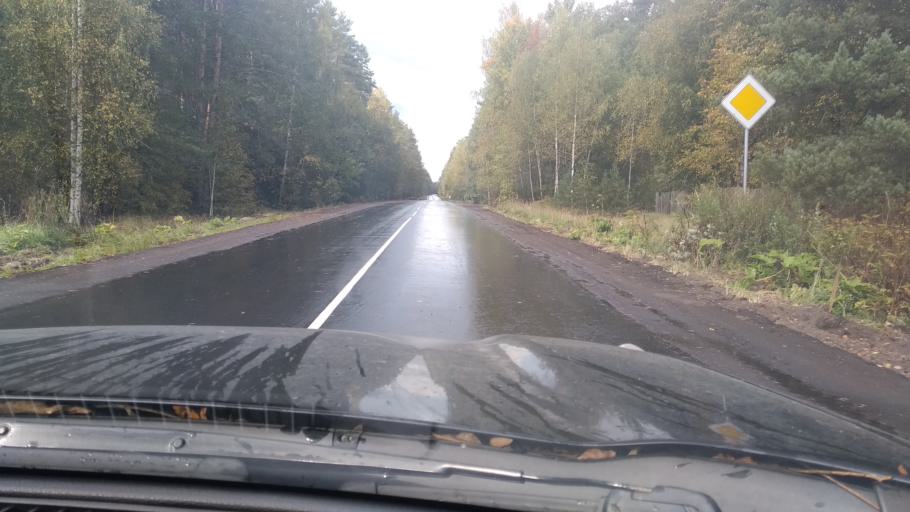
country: RU
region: Tverskaya
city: Il'inskoye
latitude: 57.2560
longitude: 37.1808
